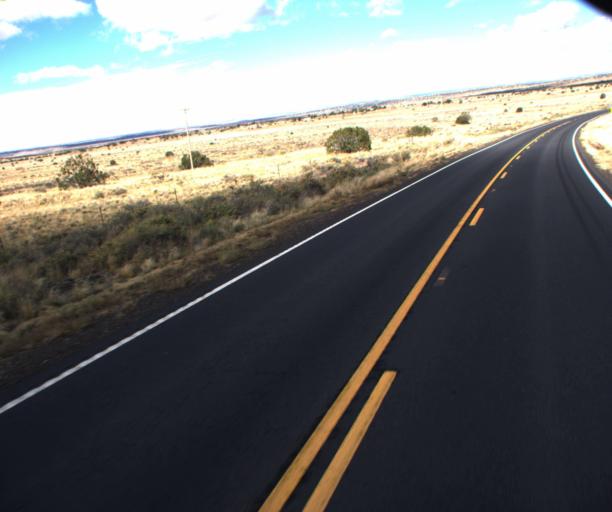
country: US
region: Arizona
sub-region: Apache County
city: Houck
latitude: 35.0369
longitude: -109.2659
